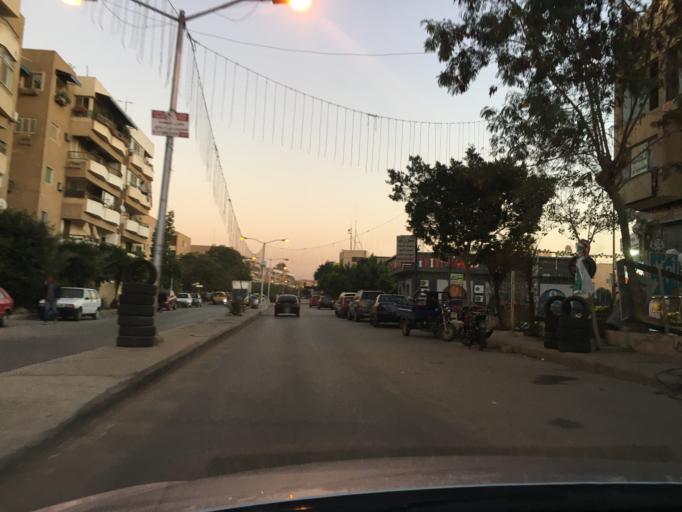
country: EG
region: Al Jizah
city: Madinat Sittah Uktubar
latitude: 29.9840
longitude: 30.9383
